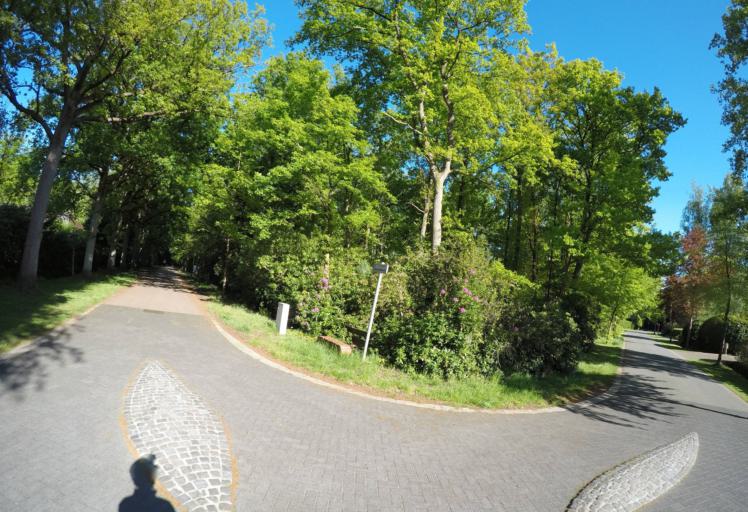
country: BE
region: Flanders
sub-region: Provincie Antwerpen
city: Schilde
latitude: 51.2618
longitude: 4.5733
